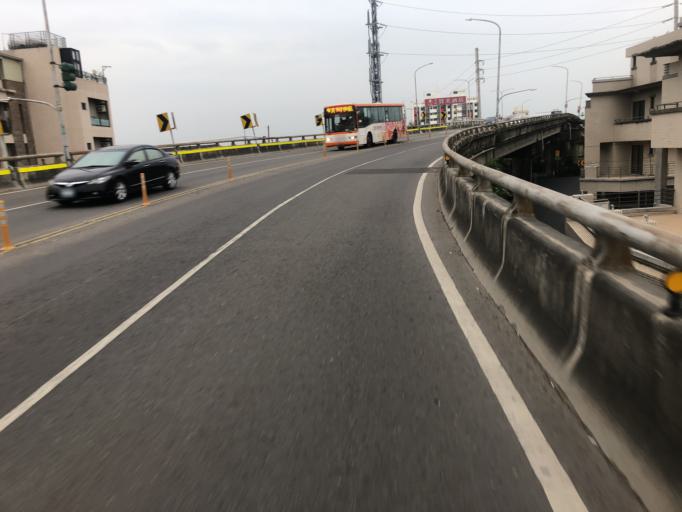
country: TW
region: Taiwan
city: Yujing
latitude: 23.1308
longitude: 120.3048
